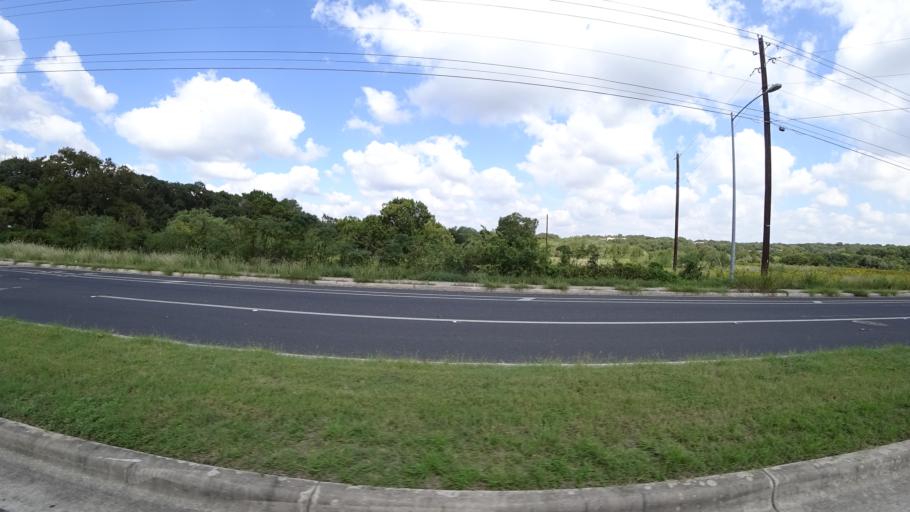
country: US
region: Texas
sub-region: Travis County
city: Manchaca
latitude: 30.1855
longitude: -97.8094
